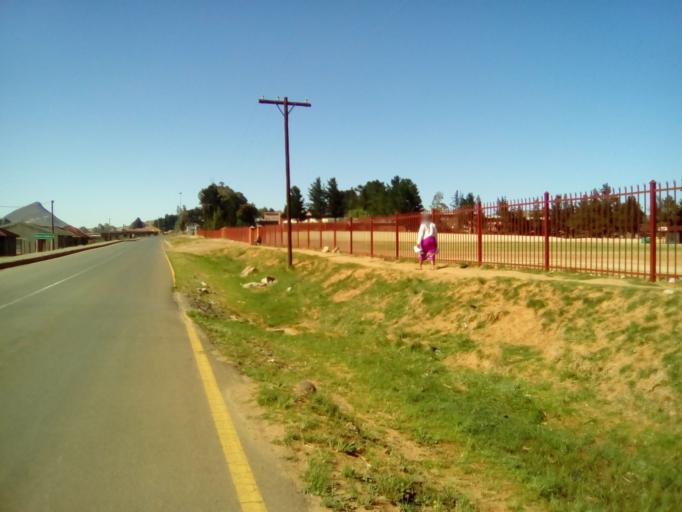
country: LS
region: Qacha's Nek
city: Qacha's Nek
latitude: -30.1095
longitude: 28.6832
